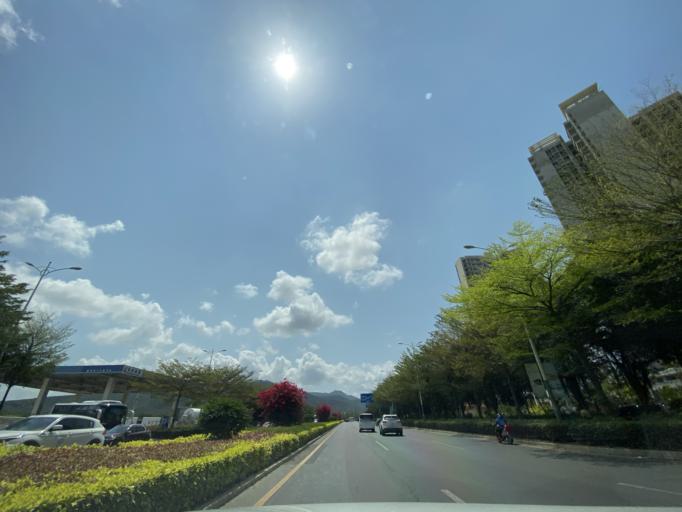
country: CN
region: Hainan
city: Tiandu
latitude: 18.2951
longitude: 109.5287
